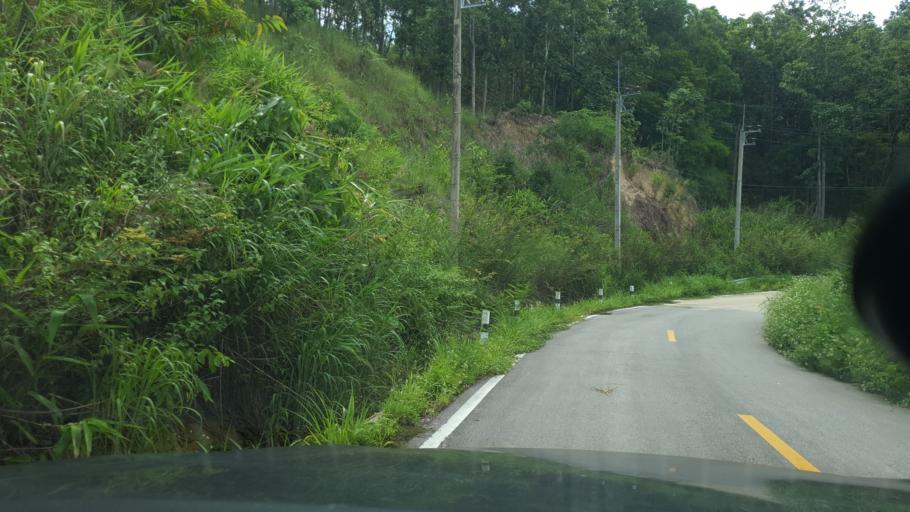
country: TH
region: Lamphun
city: Mae Tha
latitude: 18.5130
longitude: 99.2629
